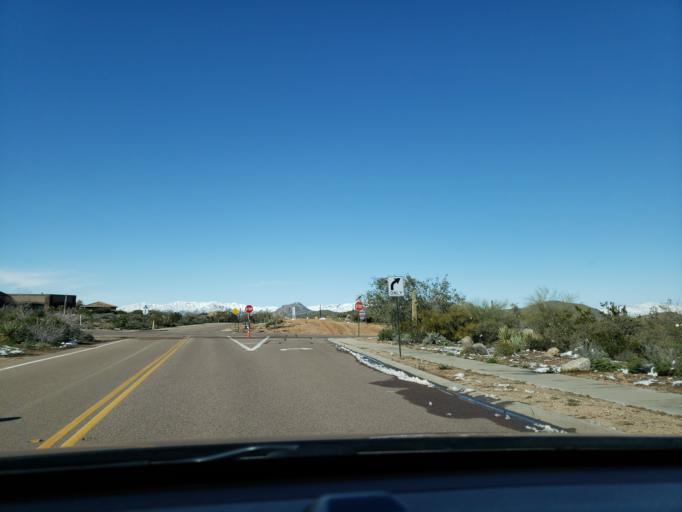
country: US
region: Arizona
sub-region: Maricopa County
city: Carefree
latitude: 33.7263
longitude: -111.8265
